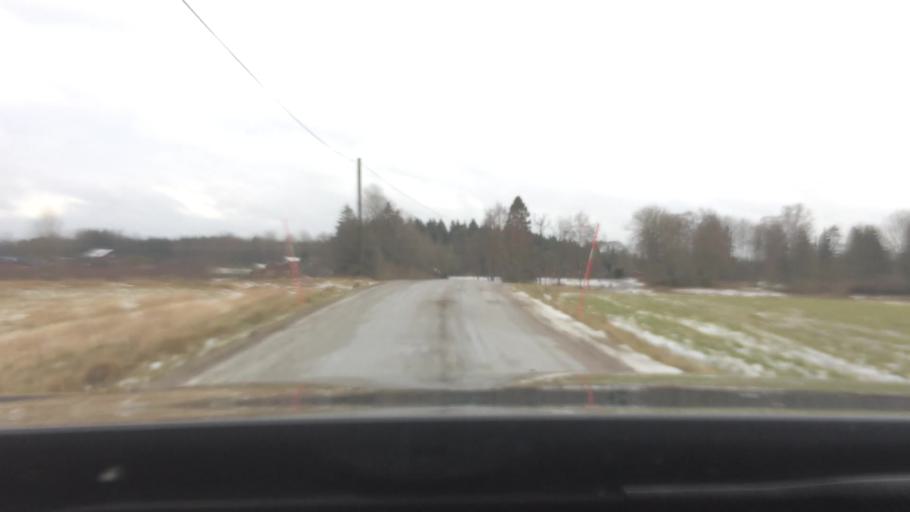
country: SE
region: Vaestra Goetaland
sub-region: Falkopings Kommun
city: Floby
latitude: 57.9916
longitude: 13.4042
